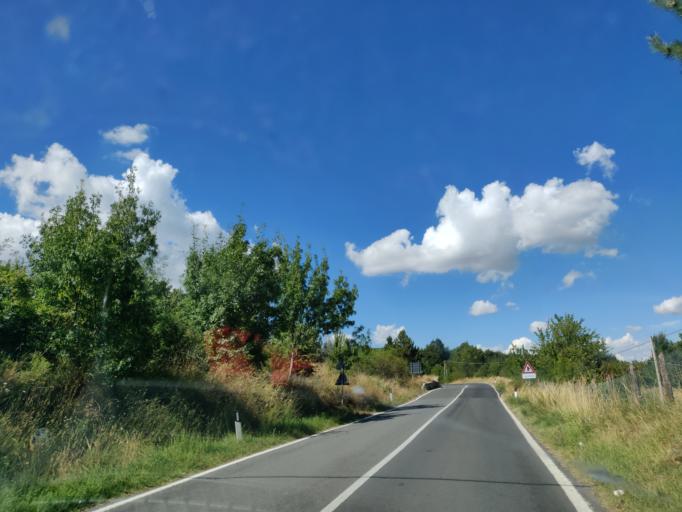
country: IT
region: Tuscany
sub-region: Provincia di Siena
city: Abbadia San Salvatore
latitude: 42.8971
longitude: 11.6685
